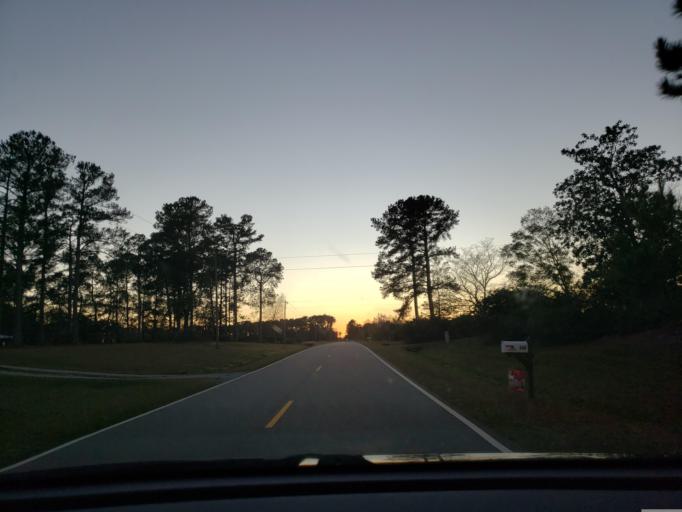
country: US
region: North Carolina
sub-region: Duplin County
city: Beulaville
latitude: 34.7566
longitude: -77.6895
